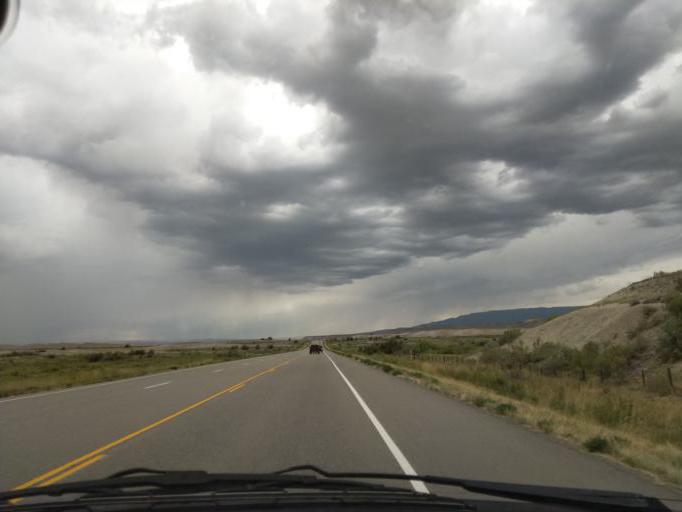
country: US
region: Colorado
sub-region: Delta County
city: Orchard City
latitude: 38.8023
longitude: -107.8708
